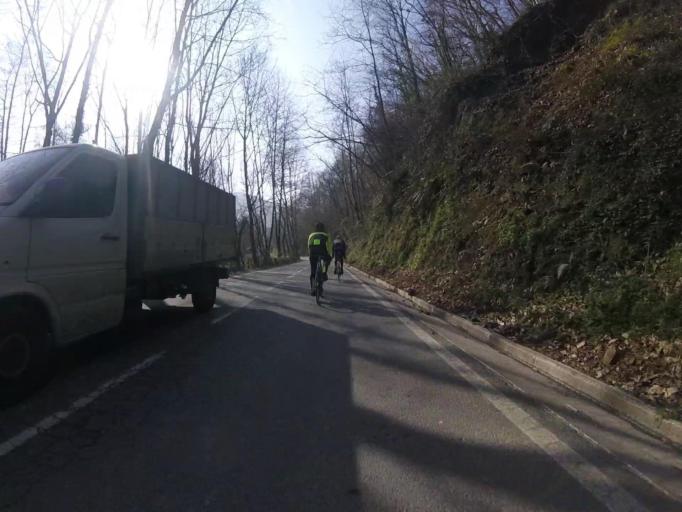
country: ES
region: Navarre
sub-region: Provincia de Navarra
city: Bera
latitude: 43.2852
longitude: -1.6796
